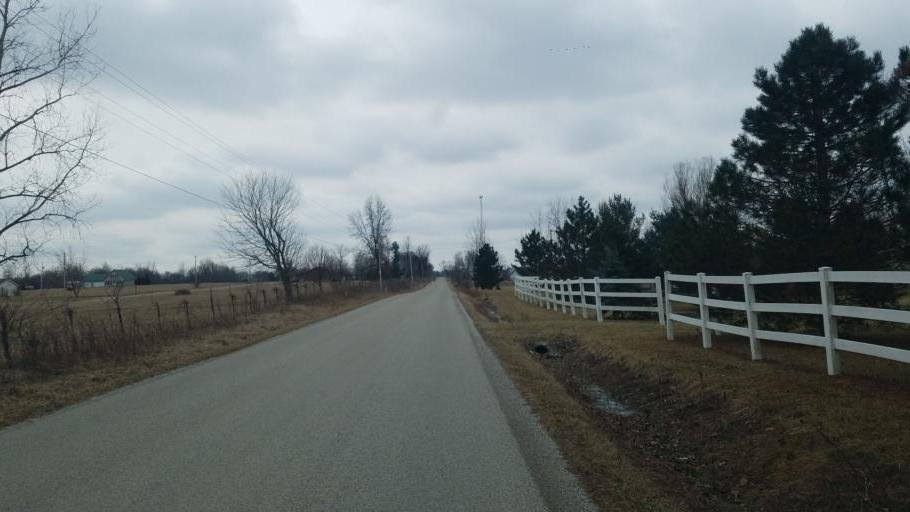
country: US
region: Ohio
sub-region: Morrow County
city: Mount Gilead
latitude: 40.6313
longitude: -82.7847
